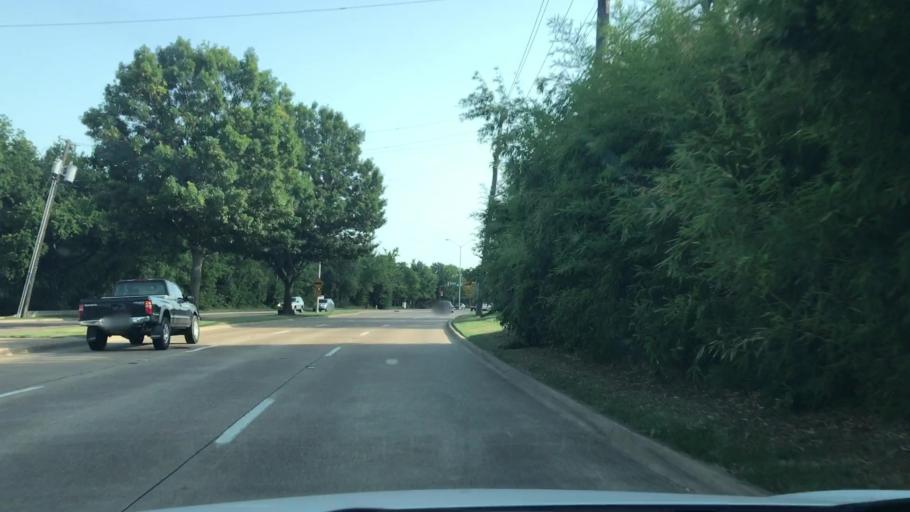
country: US
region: Texas
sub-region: Dallas County
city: Richardson
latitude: 32.8975
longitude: -96.7511
